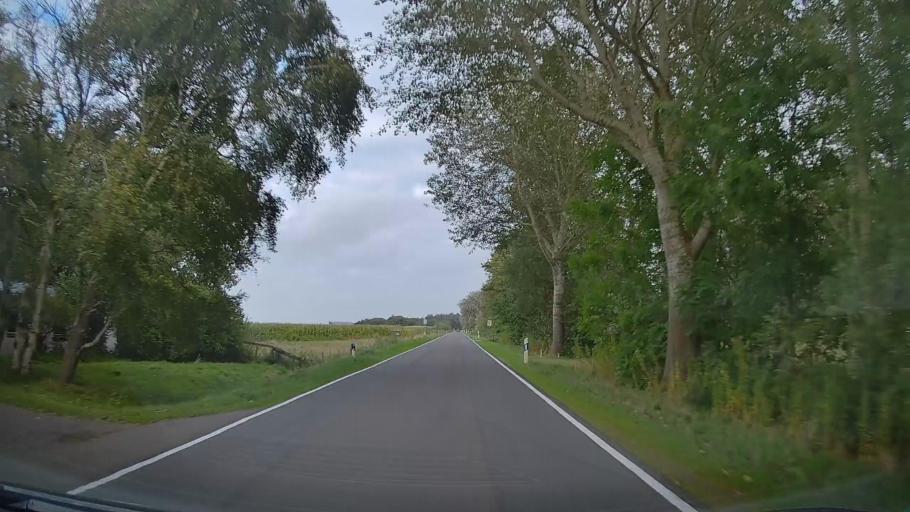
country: DE
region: Schleswig-Holstein
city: Osterhever
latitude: 54.3985
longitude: 8.7685
